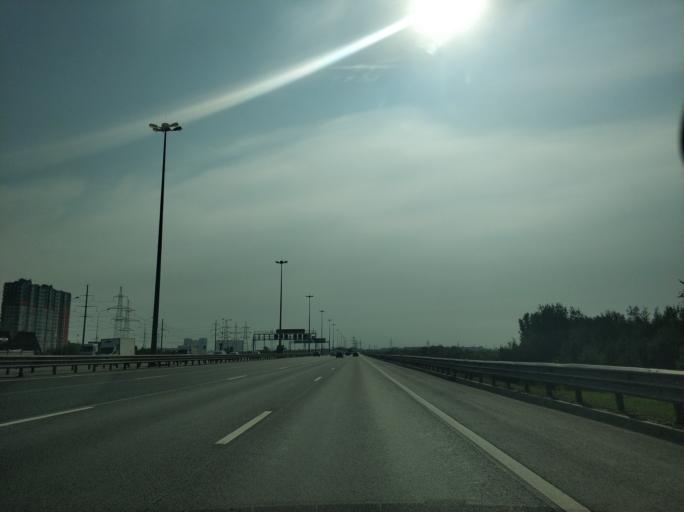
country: RU
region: Leningrad
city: Murino
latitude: 60.0283
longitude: 30.4470
